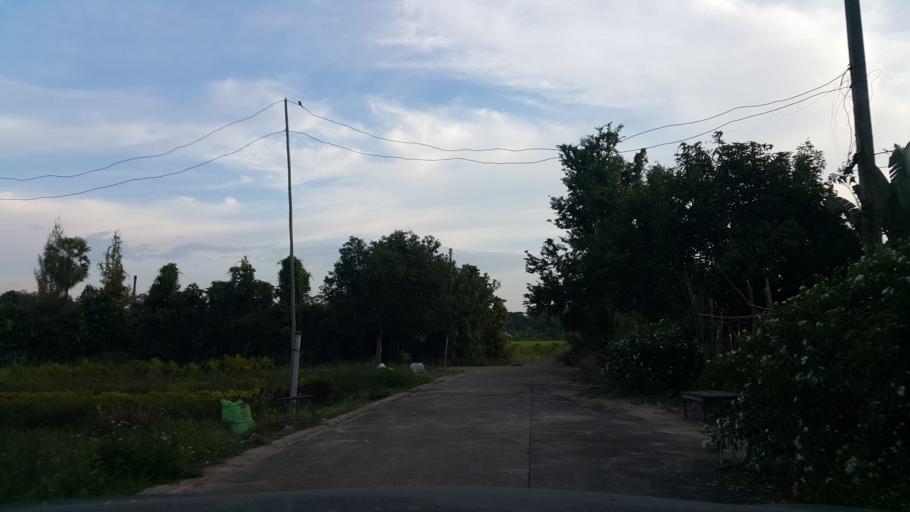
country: TH
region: Chiang Mai
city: San Sai
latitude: 18.9030
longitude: 99.0474
